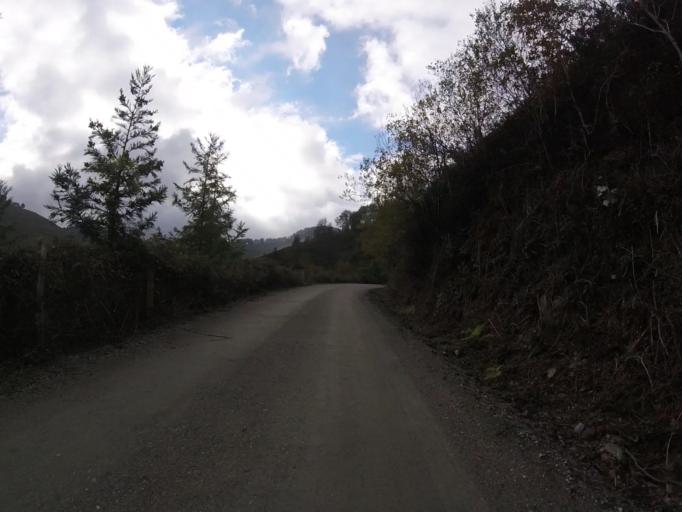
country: ES
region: Navarre
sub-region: Provincia de Navarra
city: Goizueta
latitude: 43.2181
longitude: -1.8366
